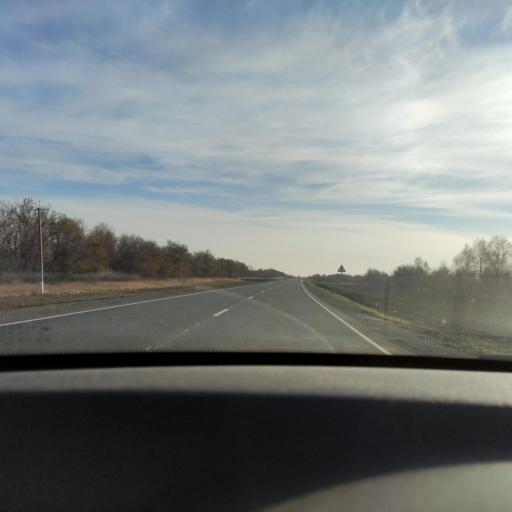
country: RU
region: Samara
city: Krasnoarmeyskoye
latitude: 52.8320
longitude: 50.0065
